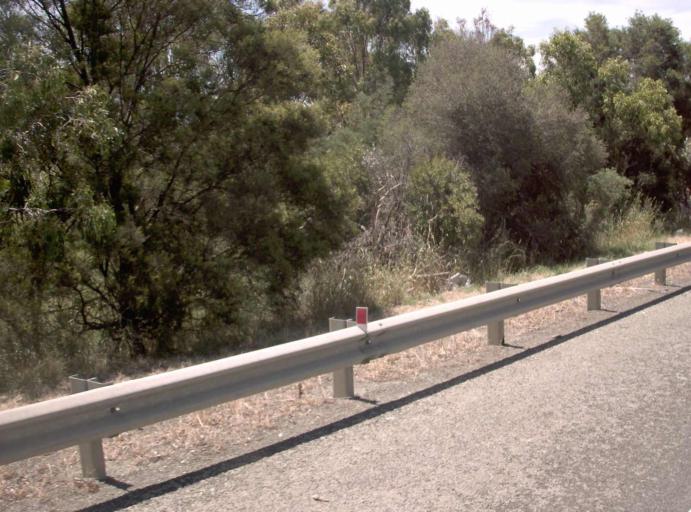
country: AU
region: Victoria
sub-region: Latrobe
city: Morwell
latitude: -38.2282
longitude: 146.4589
